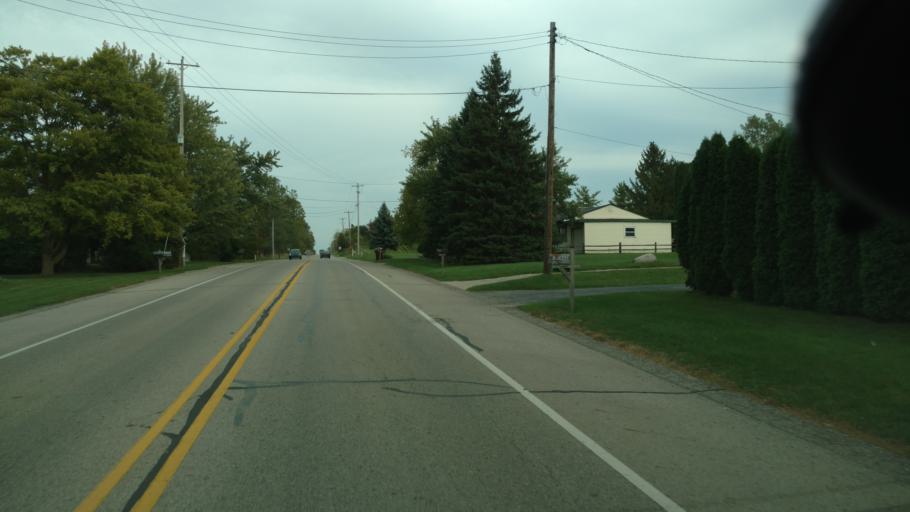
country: US
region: Michigan
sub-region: Ingham County
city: Lansing
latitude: 42.7842
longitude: -84.5346
